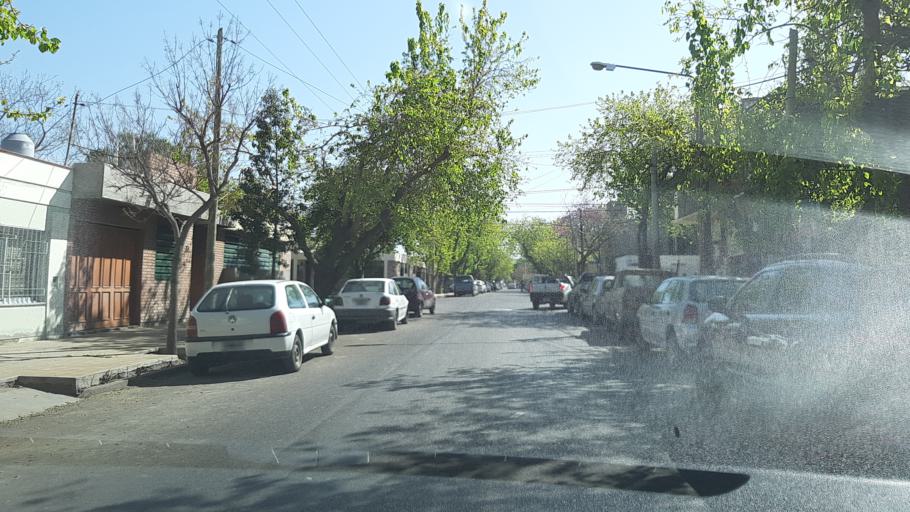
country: AR
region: San Juan
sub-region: Departamento de Santa Lucia
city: Santa Lucia
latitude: -31.5375
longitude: -68.5118
